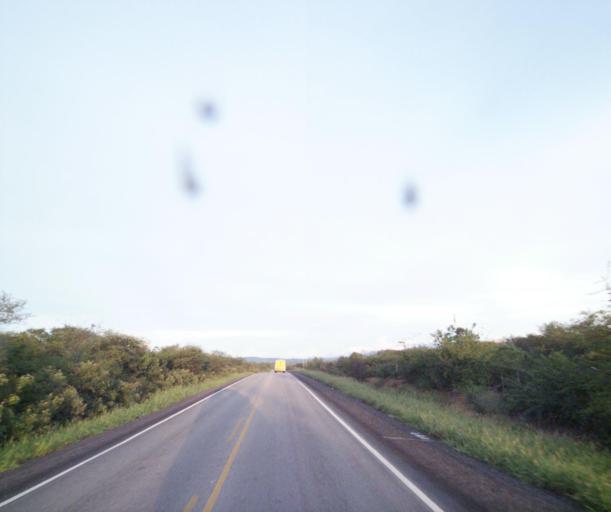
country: BR
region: Bahia
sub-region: Brumado
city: Brumado
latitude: -14.2571
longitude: -41.7720
